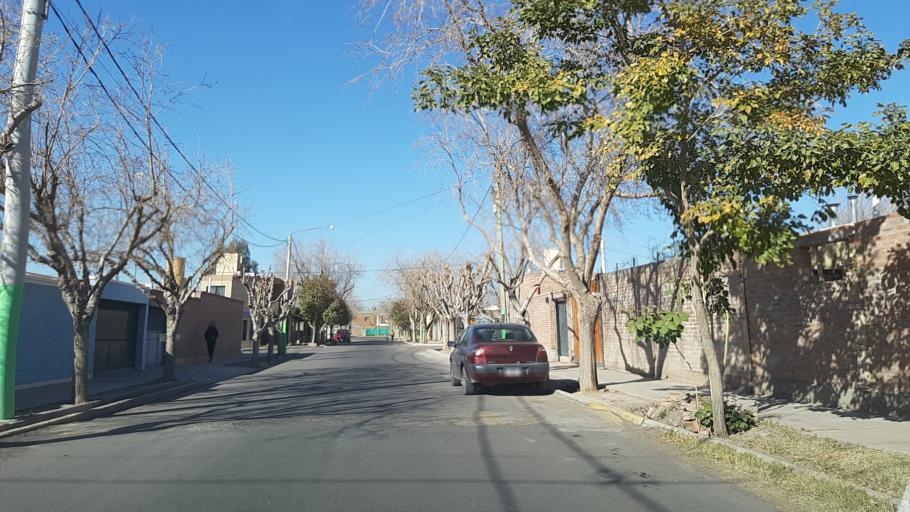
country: AR
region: San Juan
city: Villa Paula de Sarmiento
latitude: -31.5176
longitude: -68.5898
